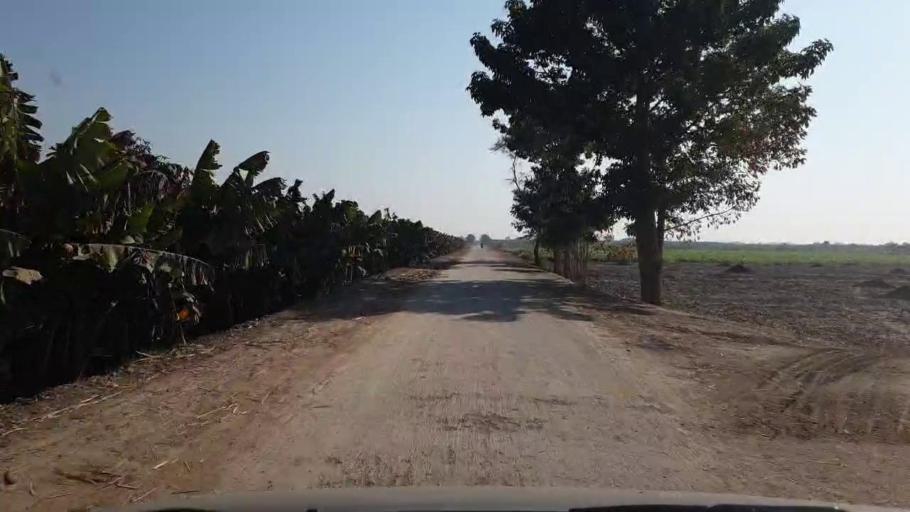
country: PK
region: Sindh
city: Tando Jam
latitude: 25.4358
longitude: 68.6083
